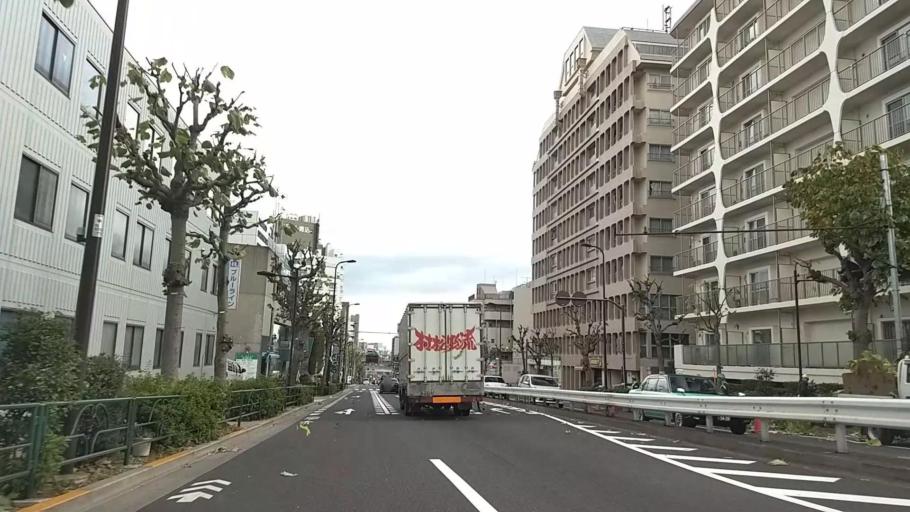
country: JP
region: Kanagawa
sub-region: Kawasaki-shi
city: Kawasaki
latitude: 35.5997
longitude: 139.7031
